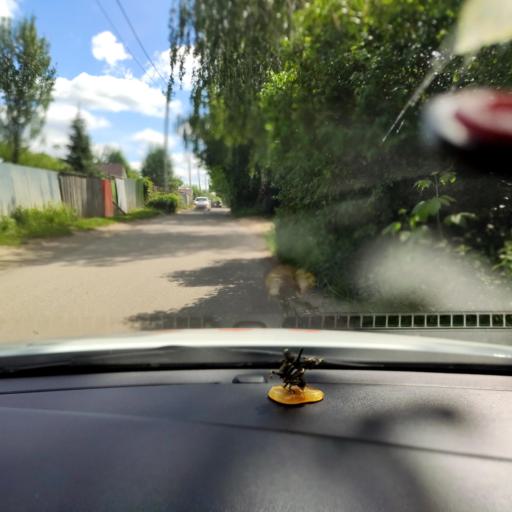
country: RU
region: Tatarstan
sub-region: Zelenodol'skiy Rayon
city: Vasil'yevo
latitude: 55.8284
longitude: 48.7486
